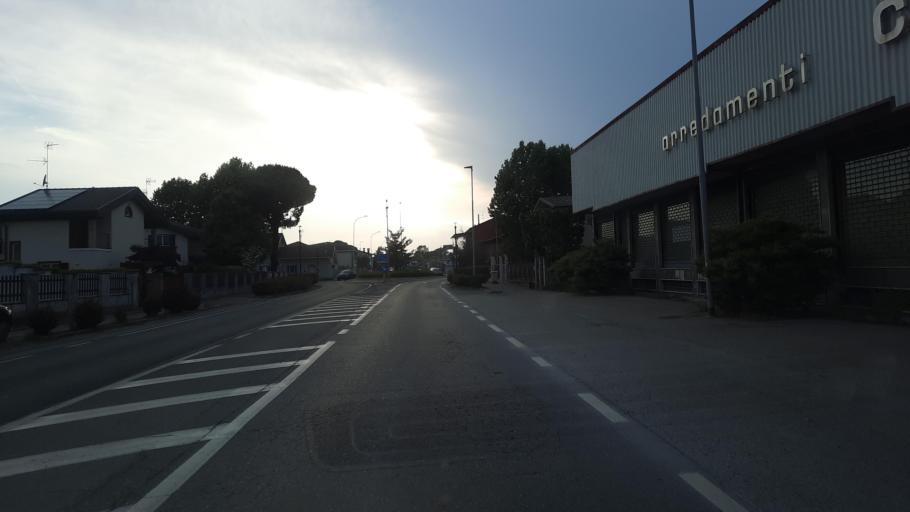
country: IT
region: Lombardy
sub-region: Provincia di Pavia
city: Garlasco
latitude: 45.1921
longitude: 8.9186
